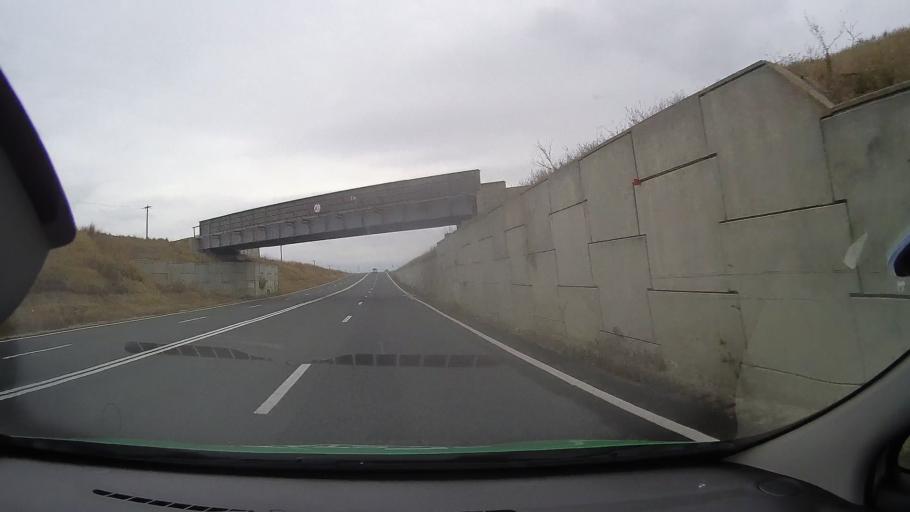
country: RO
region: Constanta
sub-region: Comuna Nicolae Balcescu
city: Nicolae Balcescu
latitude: 44.3811
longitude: 28.4056
